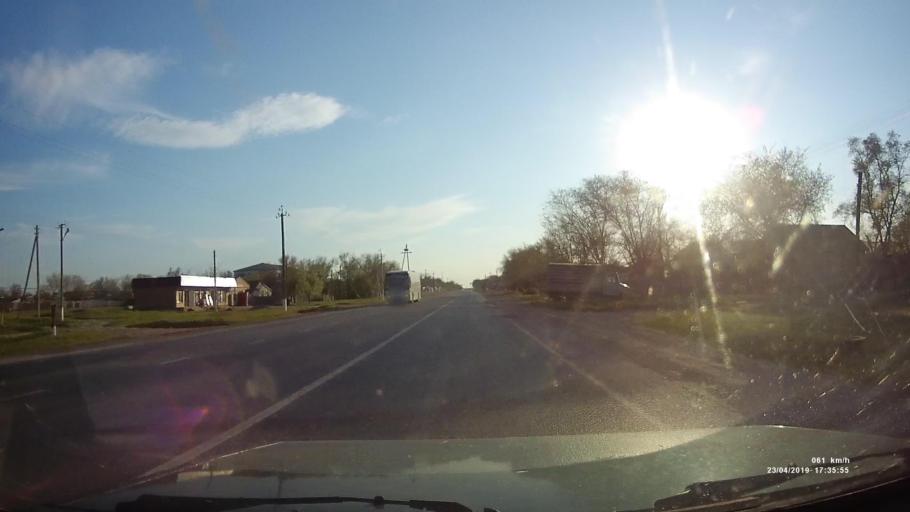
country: RU
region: Kalmykiya
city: Priyutnoye
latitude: 46.0980
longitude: 43.5131
